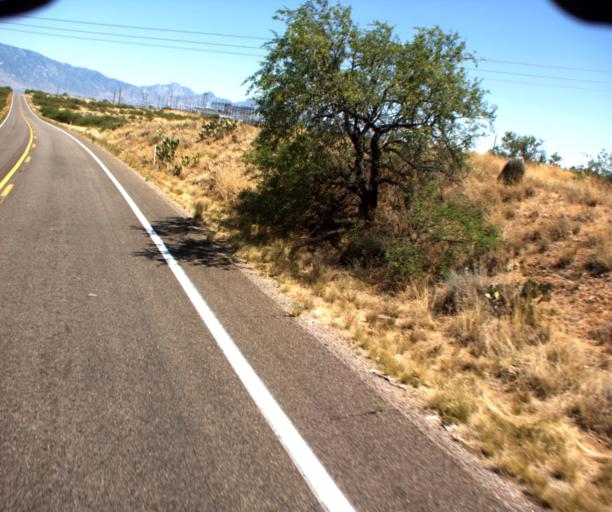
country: US
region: Arizona
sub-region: Pima County
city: Catalina
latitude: 32.6055
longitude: -110.9850
